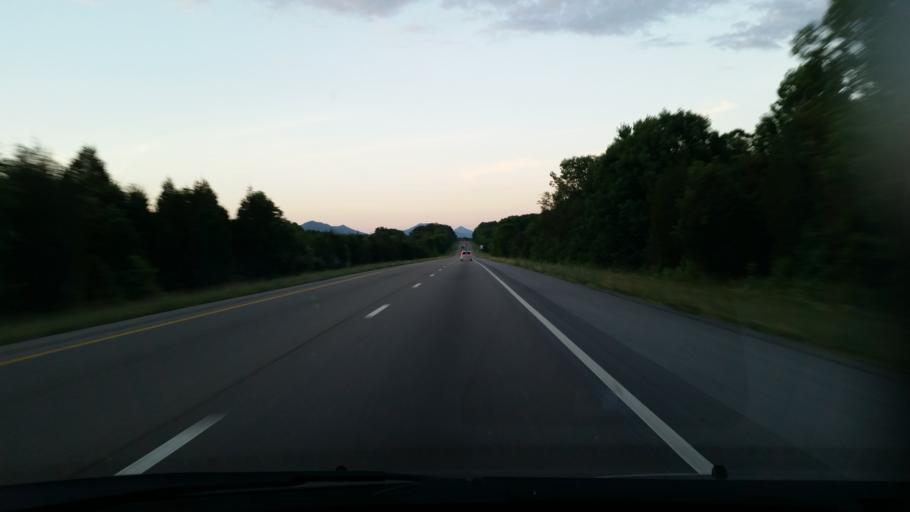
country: US
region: Tennessee
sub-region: Greene County
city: Mosheim
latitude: 36.2934
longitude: -82.8878
